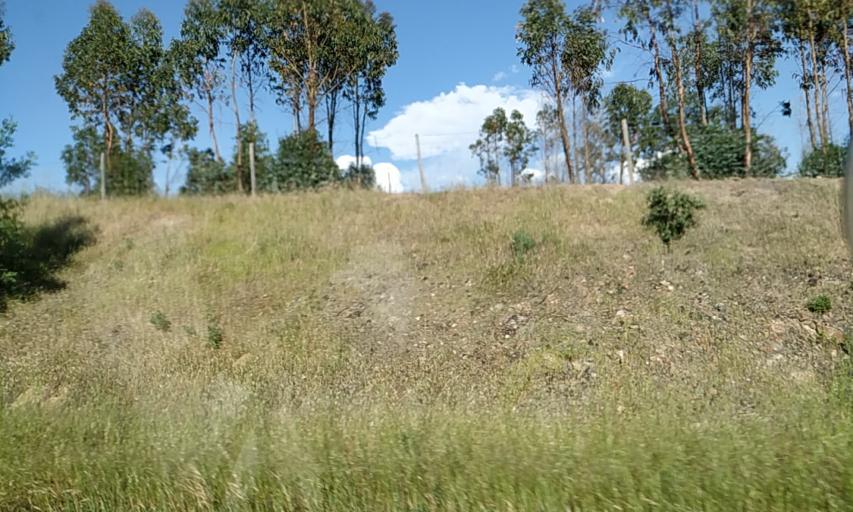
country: PT
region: Portalegre
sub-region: Fronteira
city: Fronteira
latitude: 39.0039
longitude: -7.4678
